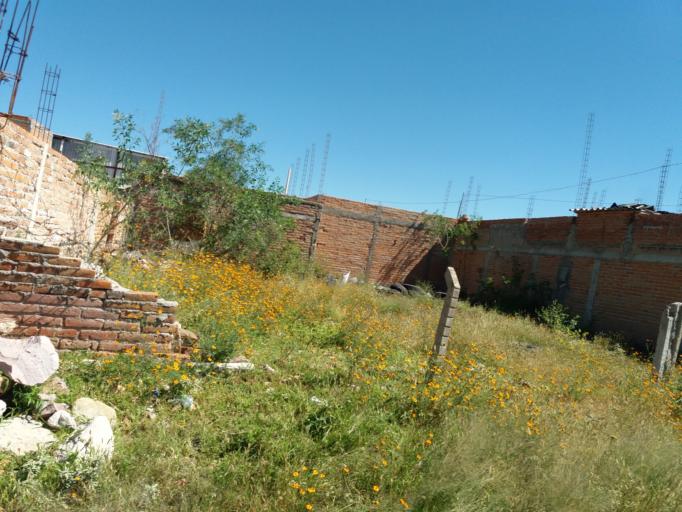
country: MX
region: Aguascalientes
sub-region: Aguascalientes
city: Aguascalientes
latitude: 21.8664
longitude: -102.2283
